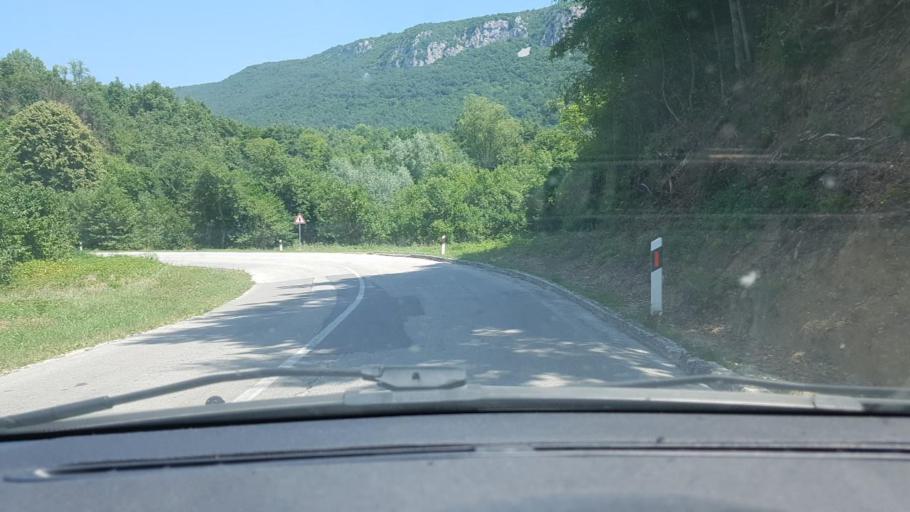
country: BA
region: Federation of Bosnia and Herzegovina
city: Orasac
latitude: 44.5912
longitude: 16.0831
